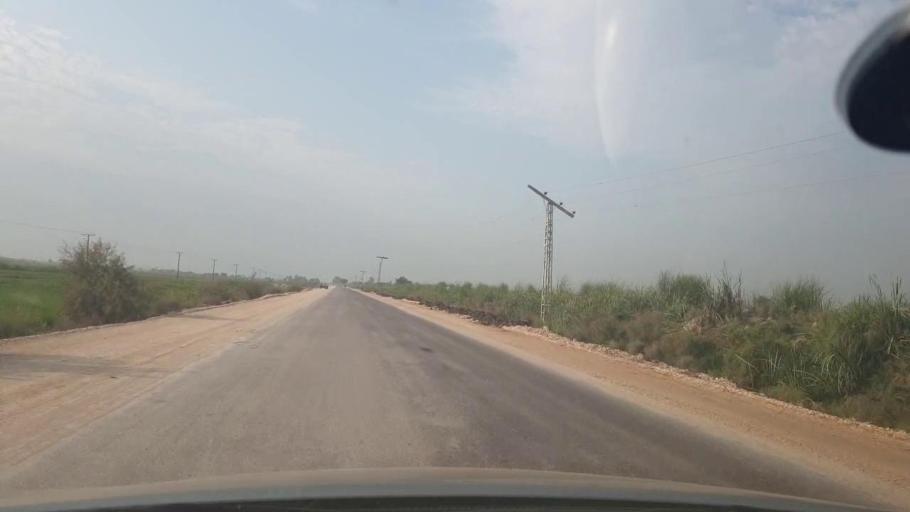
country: PK
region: Sindh
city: Jacobabad
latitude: 28.1815
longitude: 68.3675
